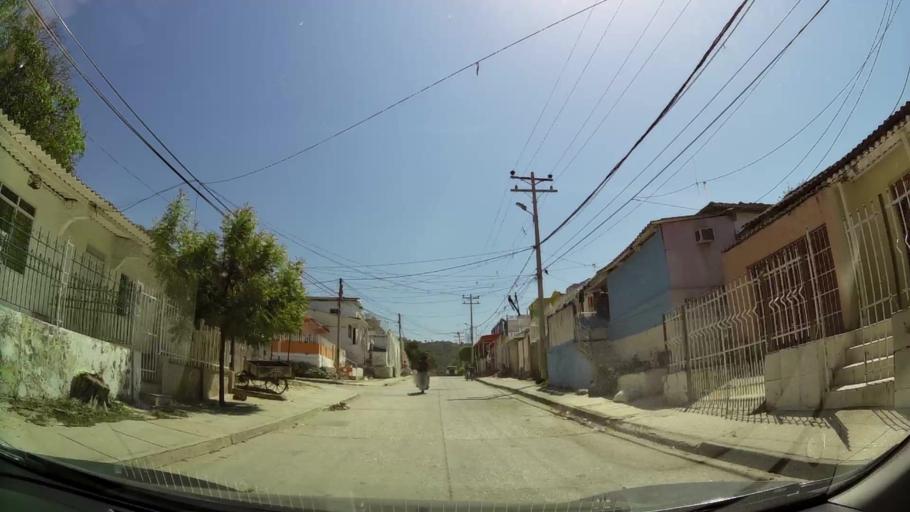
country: CO
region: Bolivar
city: Cartagena
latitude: 10.4300
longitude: -75.5310
